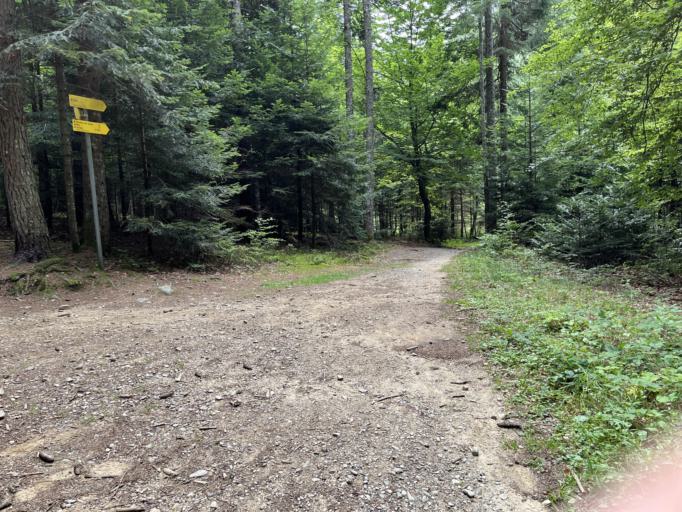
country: AT
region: Carinthia
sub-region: Politischer Bezirk Spittal an der Drau
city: Millstatt
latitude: 46.7892
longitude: 13.5522
